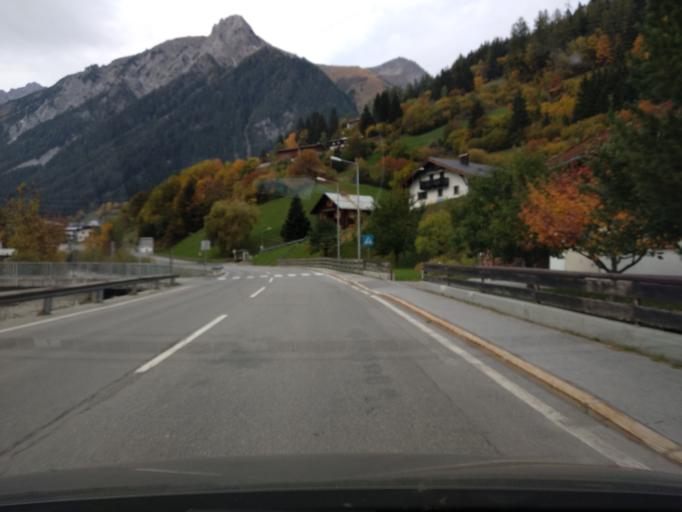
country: AT
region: Tyrol
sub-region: Politischer Bezirk Landeck
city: Flirsch
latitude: 47.1428
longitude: 10.4153
